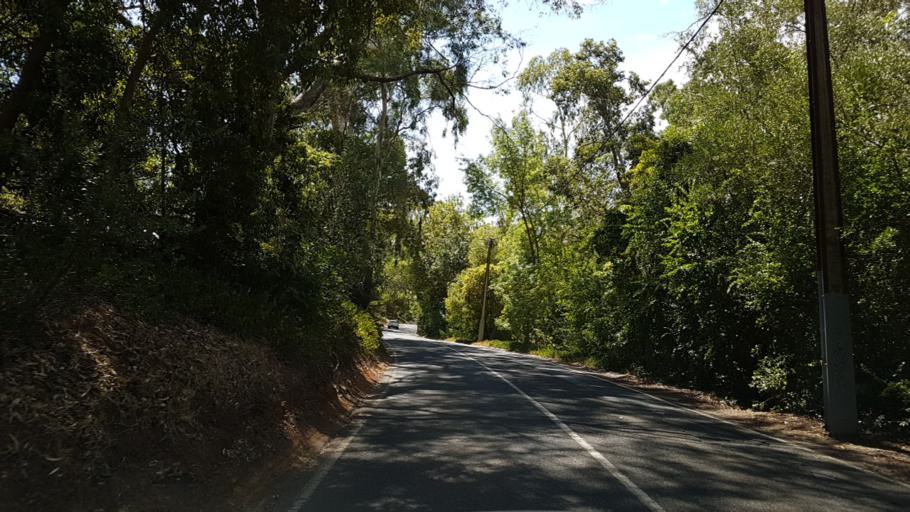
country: AU
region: South Australia
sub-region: Mitcham
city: Belair
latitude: -35.0025
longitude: 138.6328
